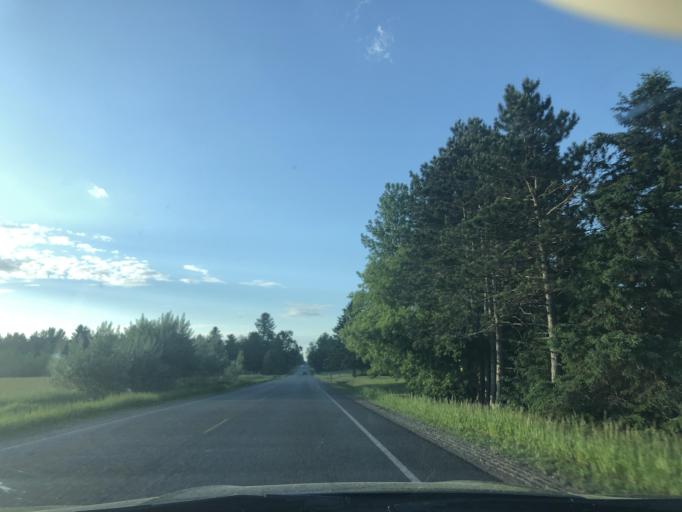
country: US
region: Michigan
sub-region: Missaukee County
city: Lake City
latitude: 44.3442
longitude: -85.0755
